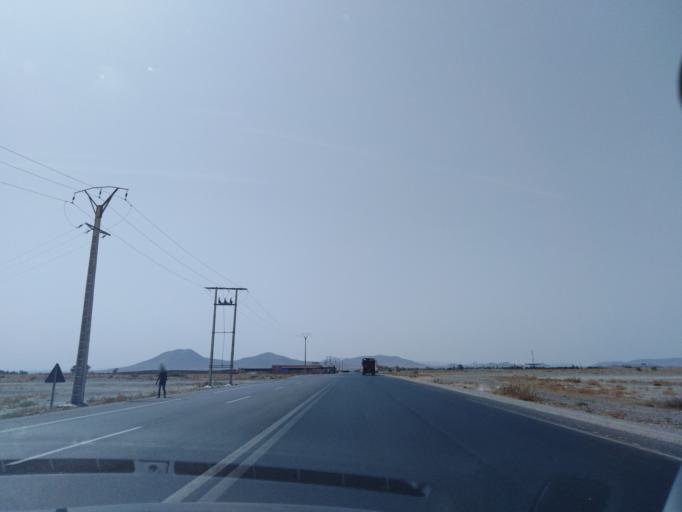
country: MA
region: Marrakech-Tensift-Al Haouz
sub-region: Marrakech
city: Marrakesh
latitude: 31.7686
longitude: -8.1240
